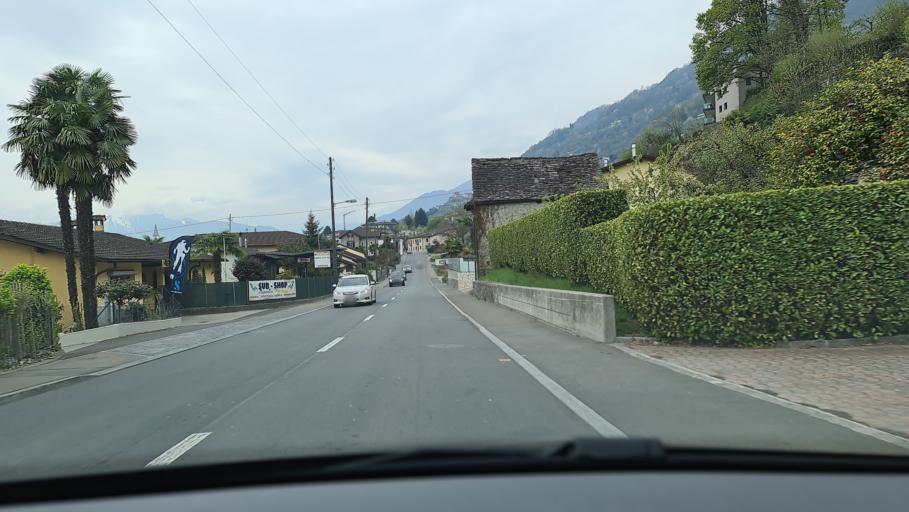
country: CH
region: Ticino
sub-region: Locarno District
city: Cugnasco
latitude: 46.1755
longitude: 8.9258
